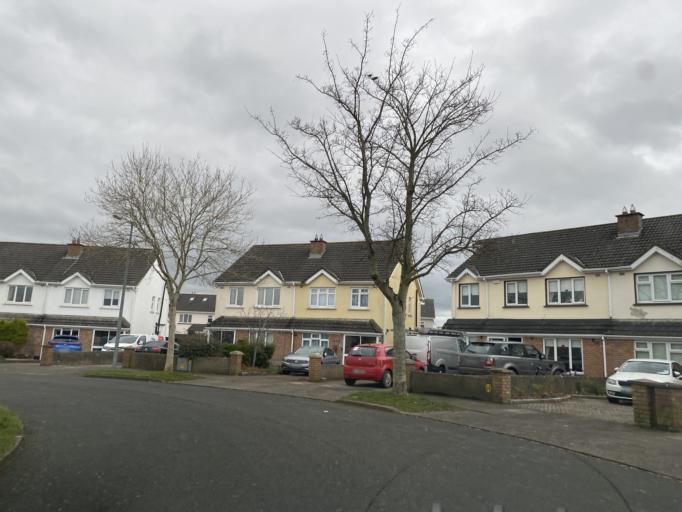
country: IE
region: Leinster
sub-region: Kildare
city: Celbridge
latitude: 53.3509
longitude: -6.5554
